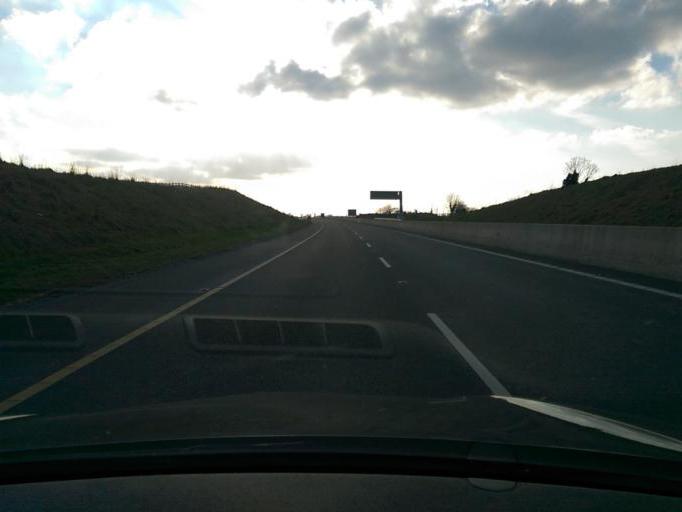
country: IE
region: Leinster
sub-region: Laois
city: Rathdowney
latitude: 52.9227
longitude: -7.6576
